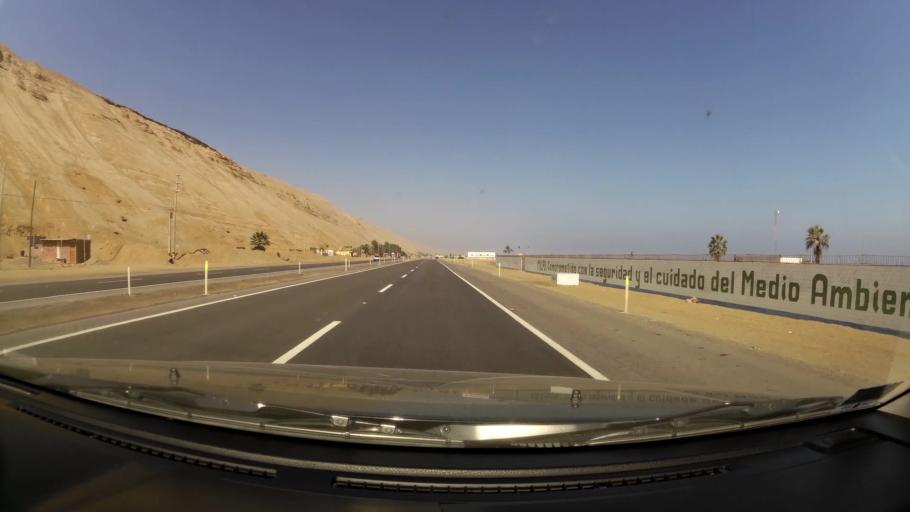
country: PE
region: Ica
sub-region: Provincia de Chincha
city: San Pedro
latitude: -13.3323
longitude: -76.2371
